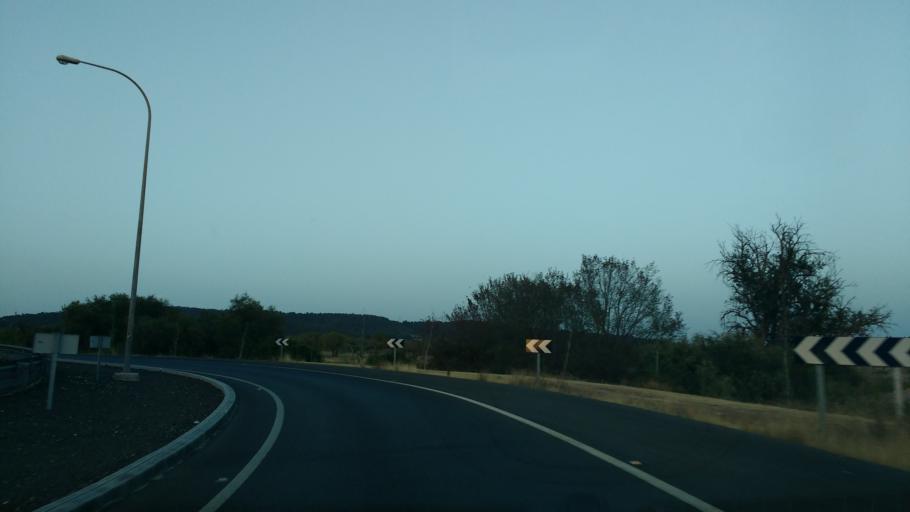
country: ES
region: Balearic Islands
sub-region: Illes Balears
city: Marratxi
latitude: 39.6290
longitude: 2.7380
